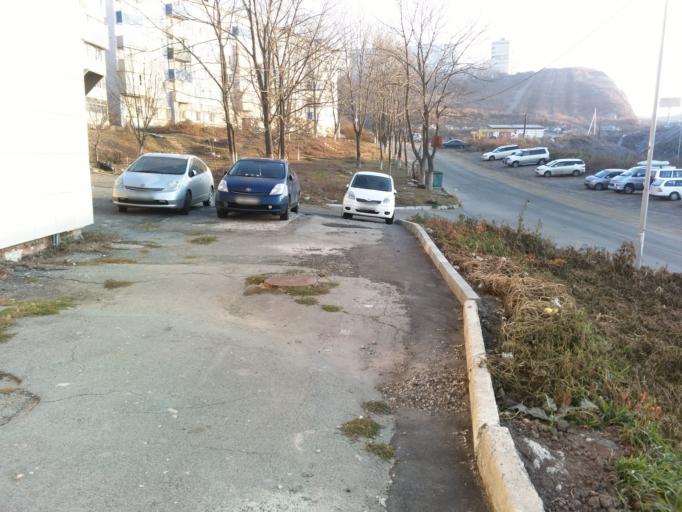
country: RU
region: Primorskiy
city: Vladivostok
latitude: 43.0892
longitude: 131.9732
